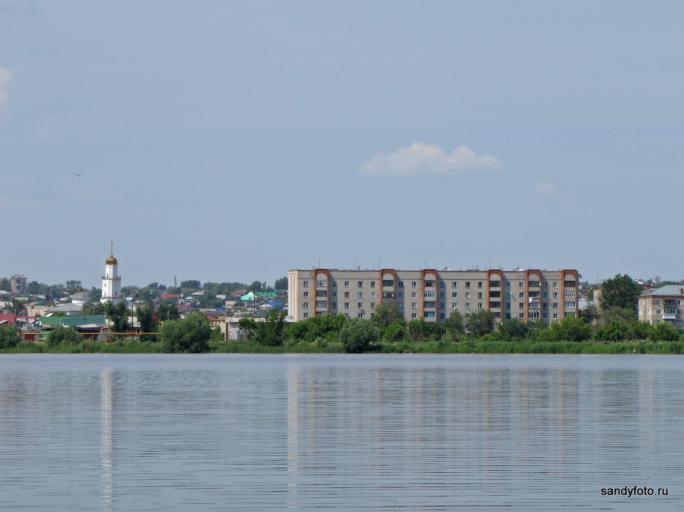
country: RU
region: Chelyabinsk
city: Troitsk
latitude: 54.0769
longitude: 61.5763
